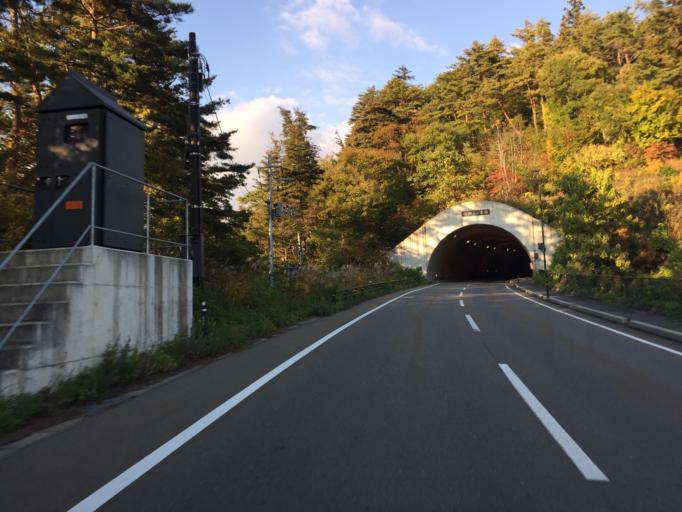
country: JP
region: Fukushima
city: Kitakata
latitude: 37.7389
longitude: 139.8801
